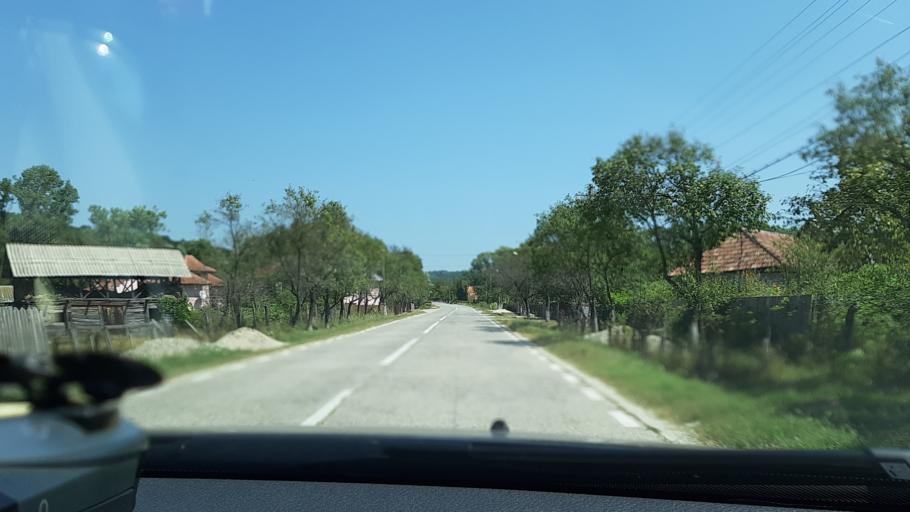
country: RO
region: Gorj
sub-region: Comuna Logresti-Mosteni
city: Logresti Mosteni
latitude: 44.9010
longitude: 23.7363
